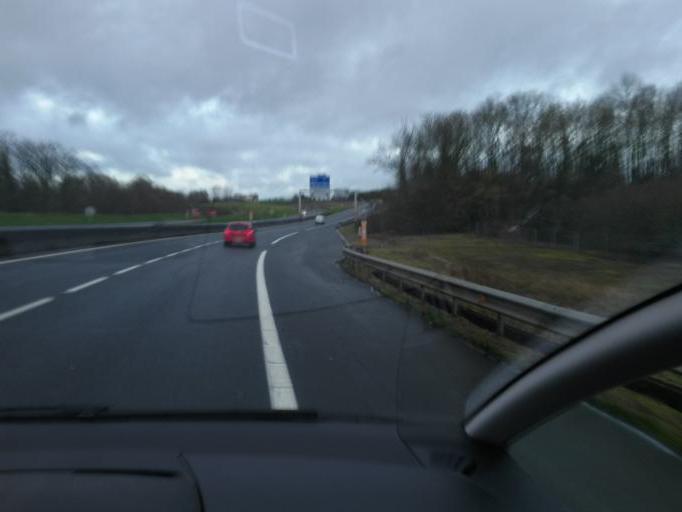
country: FR
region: Picardie
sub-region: Departement de la Somme
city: Longueau
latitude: 49.8606
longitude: 2.3783
